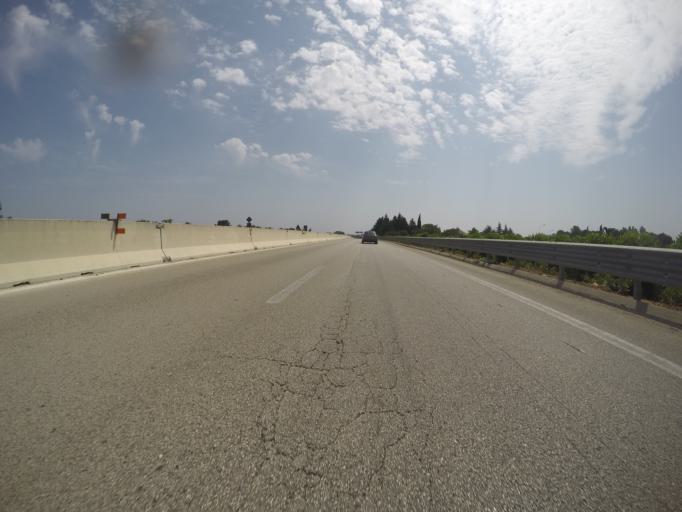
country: IT
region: Apulia
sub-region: Provincia di Brindisi
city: Mesagne
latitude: 40.5663
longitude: 17.7796
